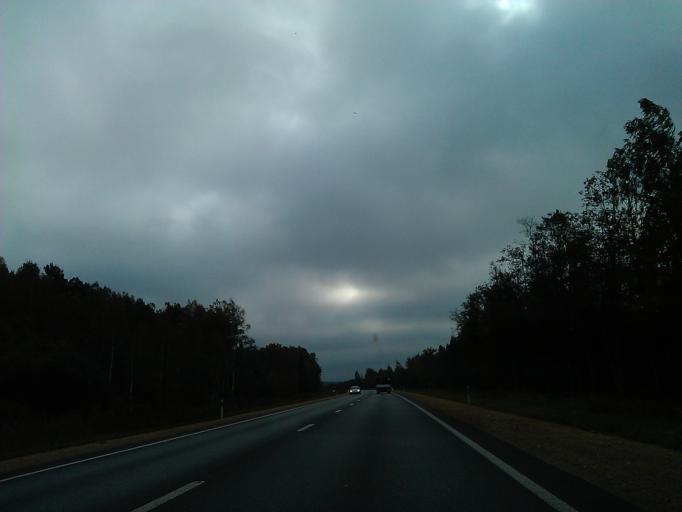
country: LV
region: Aizkraukles Rajons
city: Aizkraukle
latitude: 56.7097
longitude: 25.2252
